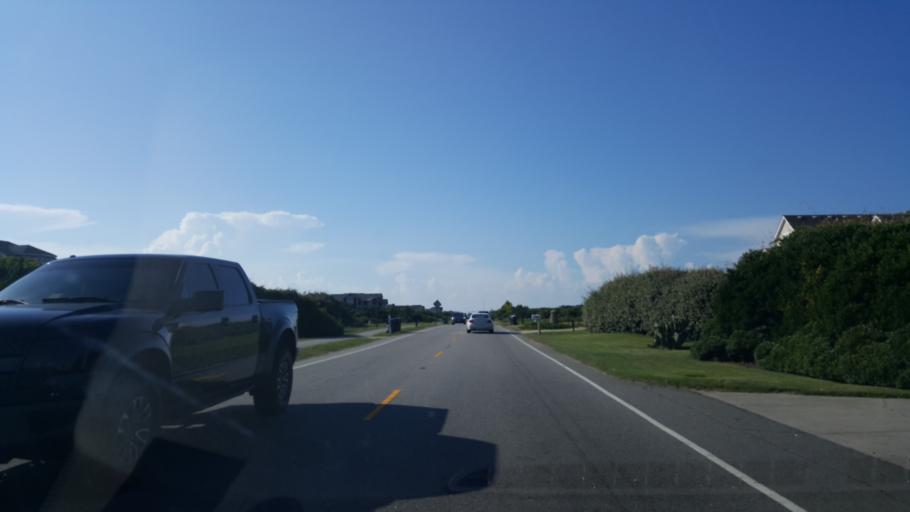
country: US
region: North Carolina
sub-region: Dare County
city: Southern Shores
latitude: 36.1089
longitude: -75.7169
